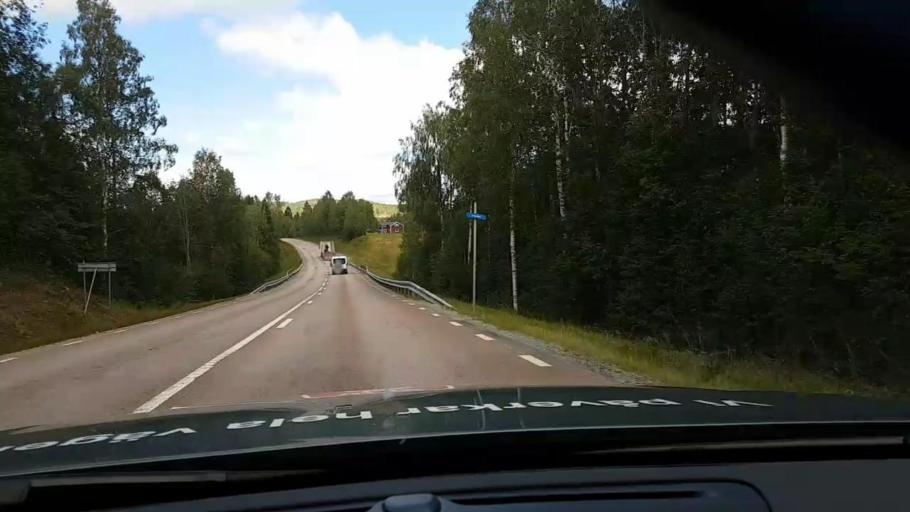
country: SE
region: Vaesternorrland
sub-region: OErnskoeldsviks Kommun
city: Bjasta
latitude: 63.3719
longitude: 18.4367
